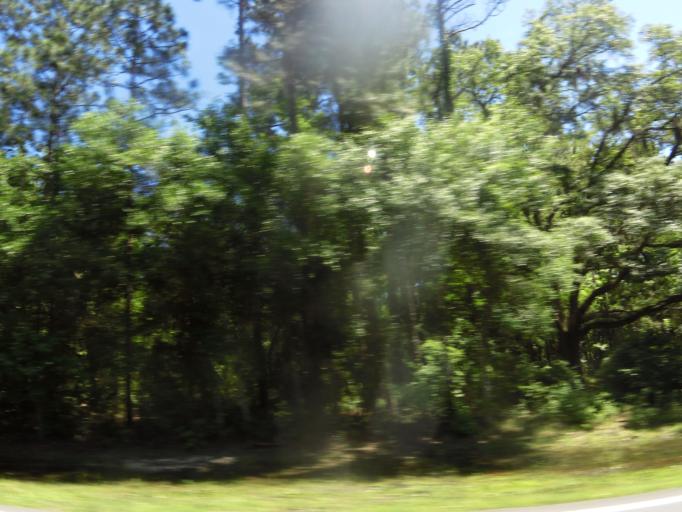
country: US
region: Florida
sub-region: Clay County
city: Green Cove Springs
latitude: 30.0187
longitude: -81.6017
